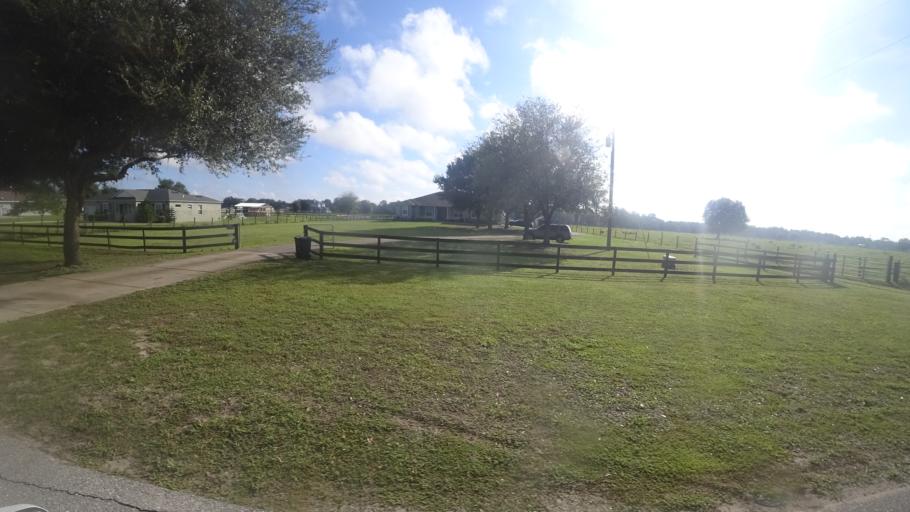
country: US
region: Florida
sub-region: Manatee County
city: Ellenton
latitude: 27.5689
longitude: -82.4089
